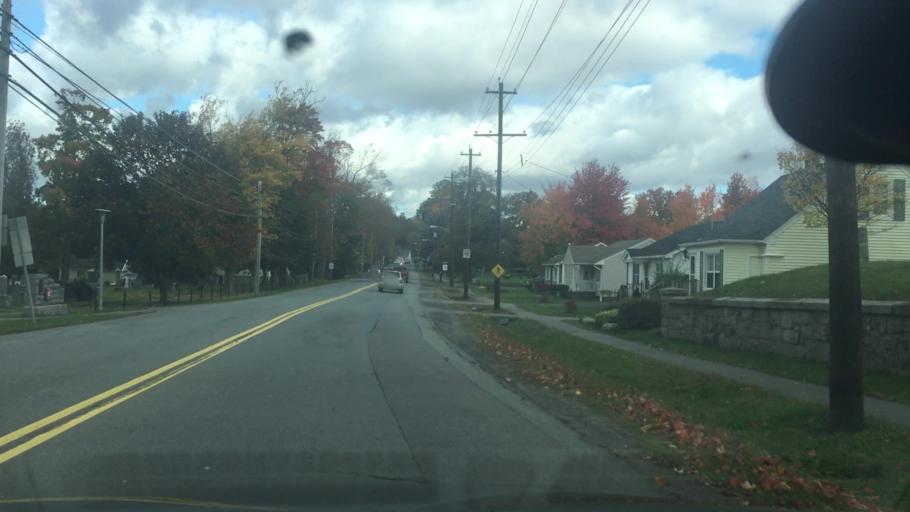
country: CA
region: Nova Scotia
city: Windsor
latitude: 44.9811
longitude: -64.1299
